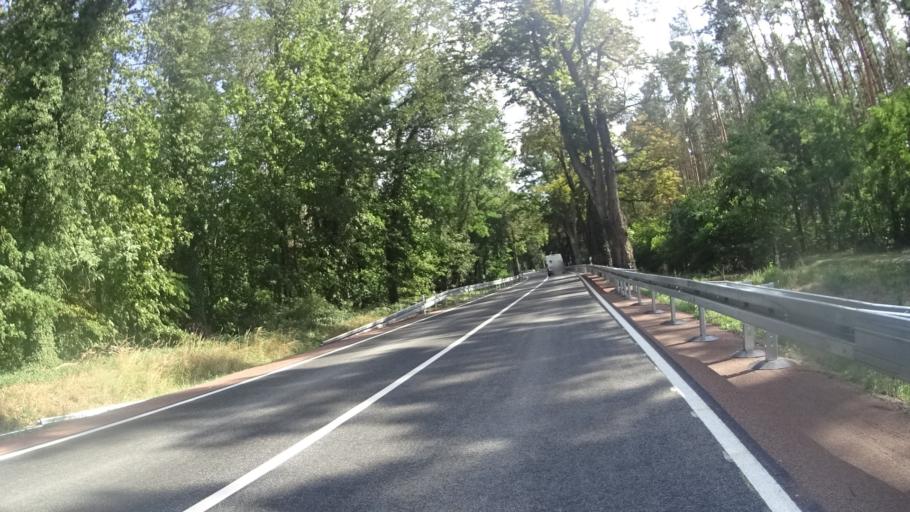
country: DE
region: Brandenburg
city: Rhinow
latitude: 52.7399
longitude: 12.3371
